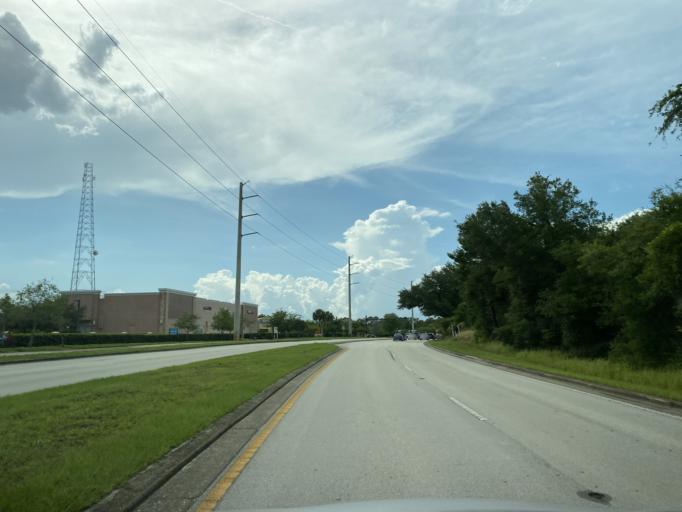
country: US
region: Florida
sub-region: Volusia County
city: Deltona
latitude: 28.8720
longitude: -81.1633
